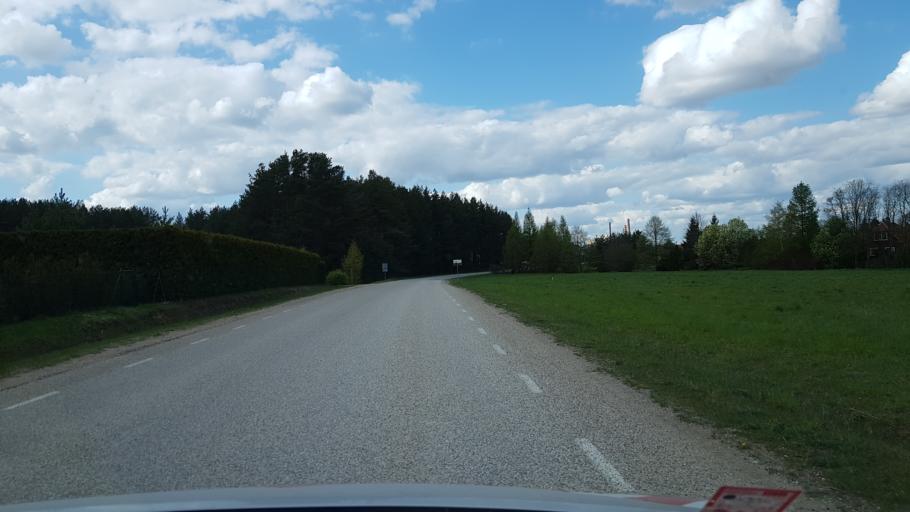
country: EE
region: Tartu
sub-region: Tartu linn
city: Tartu
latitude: 58.3561
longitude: 26.7984
